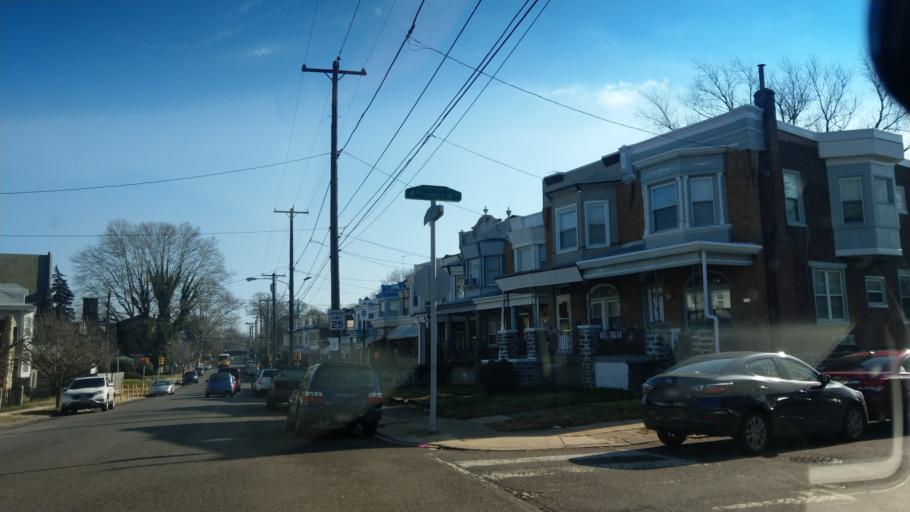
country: US
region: Pennsylvania
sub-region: Montgomery County
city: Rockledge
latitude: 40.0342
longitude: -75.1291
